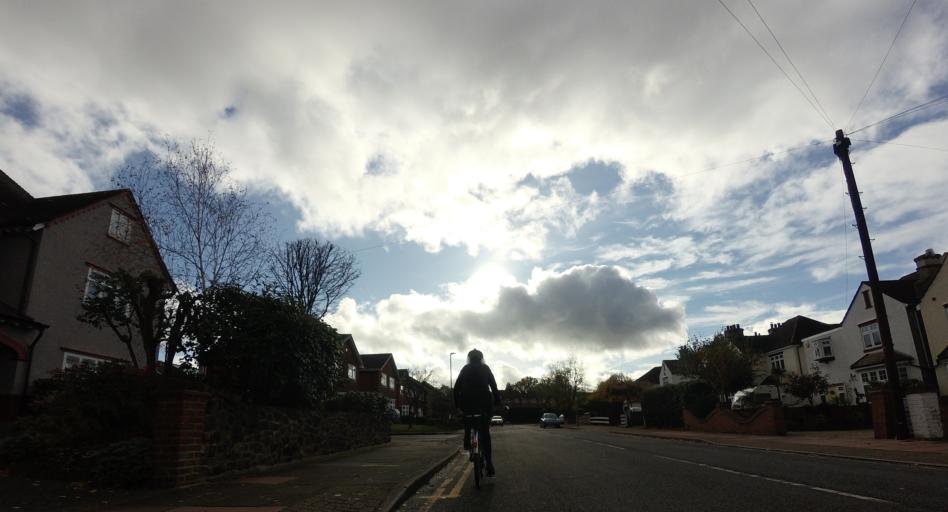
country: GB
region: England
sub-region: Greater London
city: Sidcup
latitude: 51.4315
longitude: 0.1135
